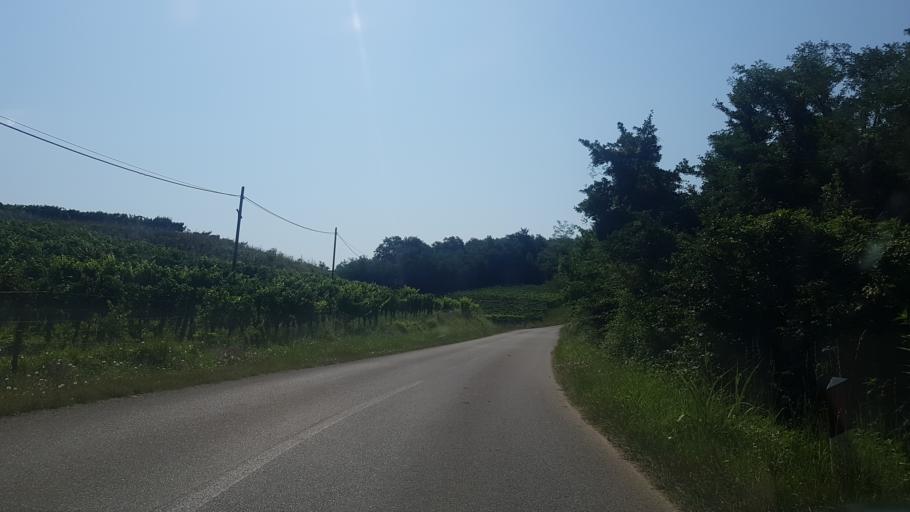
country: IT
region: Friuli Venezia Giulia
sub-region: Provincia di Gorizia
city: Mossa
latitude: 45.9608
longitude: 13.5614
